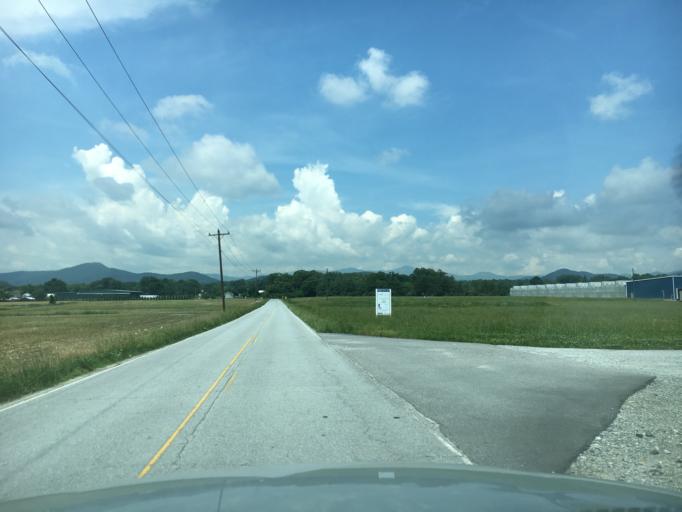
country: US
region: North Carolina
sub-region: Henderson County
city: Mills River
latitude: 35.3775
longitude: -82.5526
